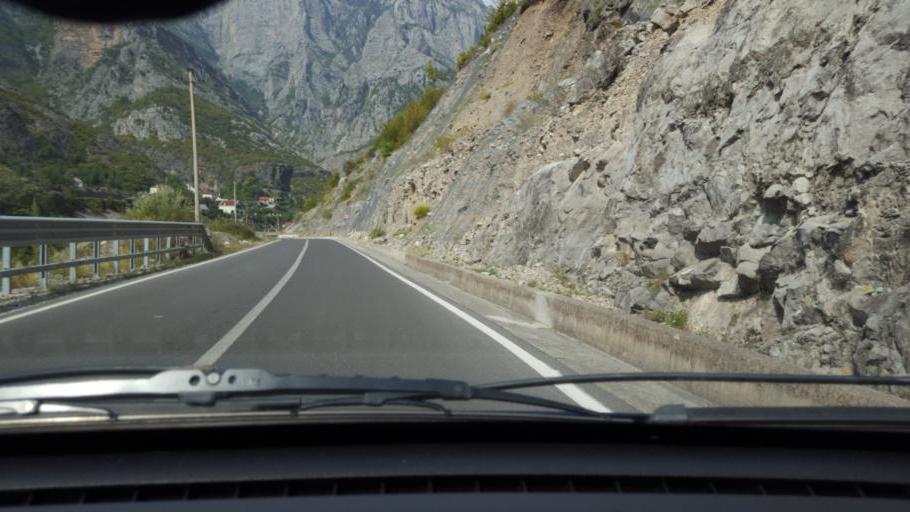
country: AL
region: Shkoder
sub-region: Rrethi i Malesia e Madhe
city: Kastrat
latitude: 42.4572
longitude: 19.5613
